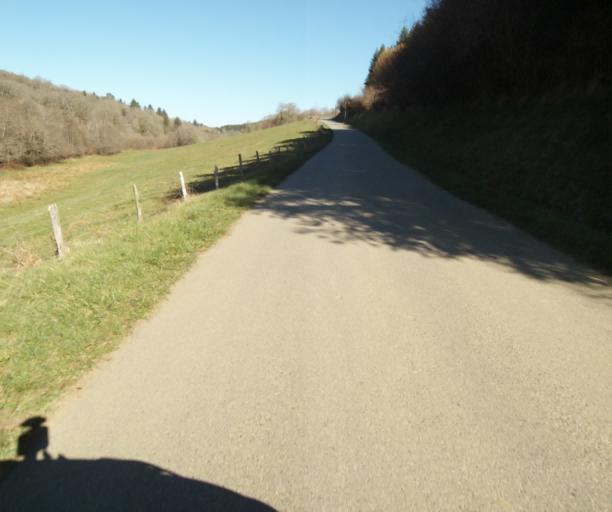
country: FR
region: Limousin
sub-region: Departement de la Correze
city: Seilhac
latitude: 45.3798
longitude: 1.7502
